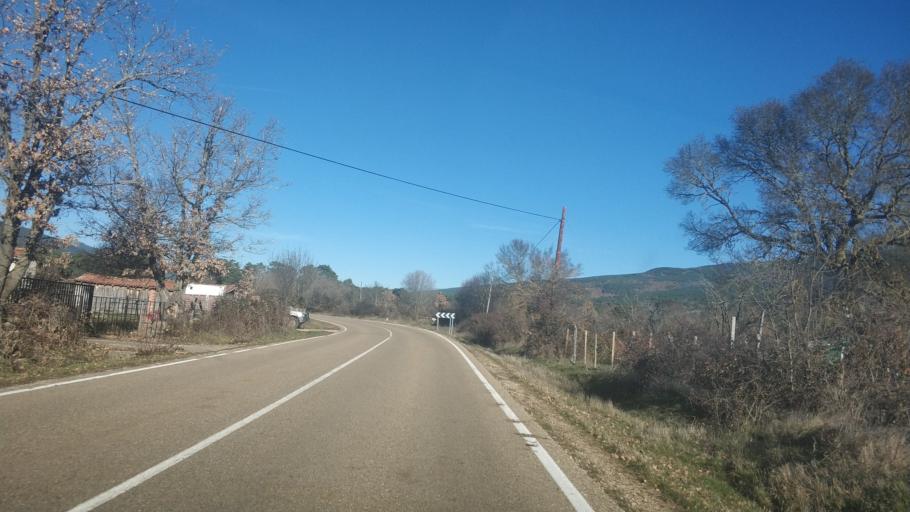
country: ES
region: Castille and Leon
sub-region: Provincia de Soria
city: Vinuesa
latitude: 41.9154
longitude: -2.7545
